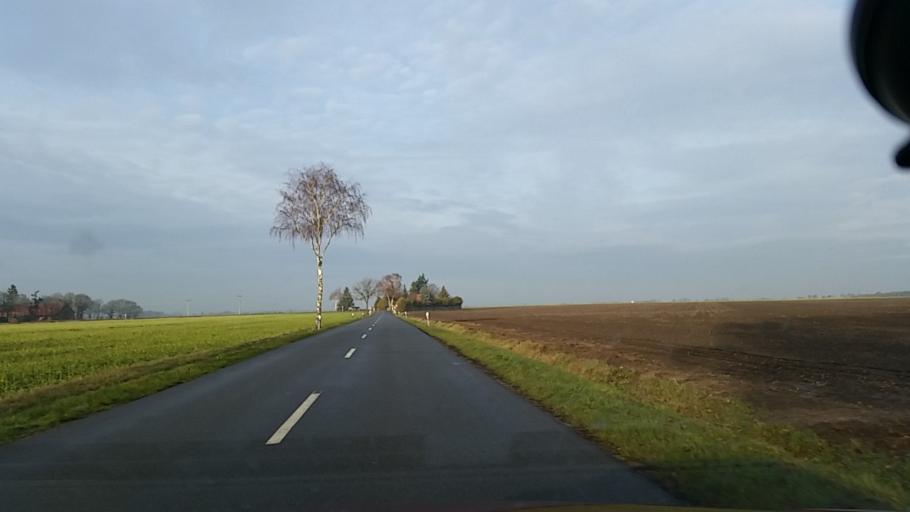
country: DE
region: Lower Saxony
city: Luder
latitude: 52.8021
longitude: 10.6964
